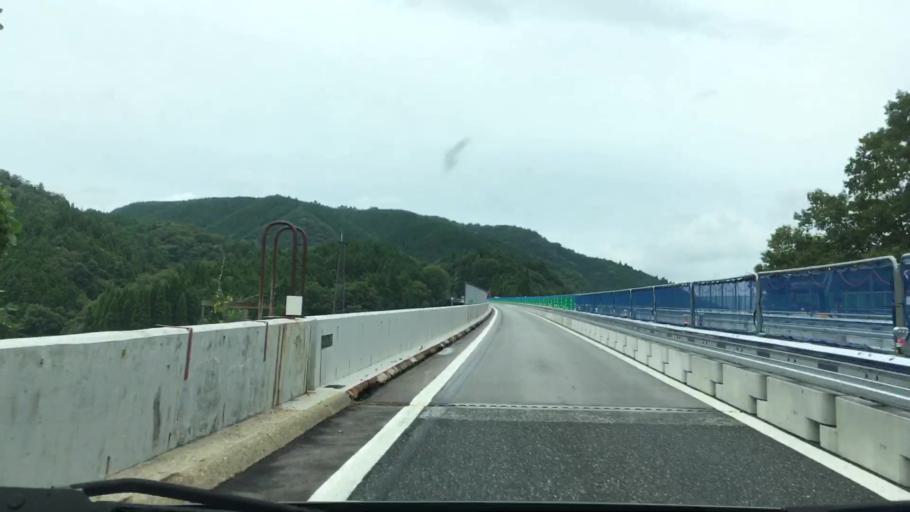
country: JP
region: Okayama
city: Niimi
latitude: 35.0289
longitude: 133.5774
